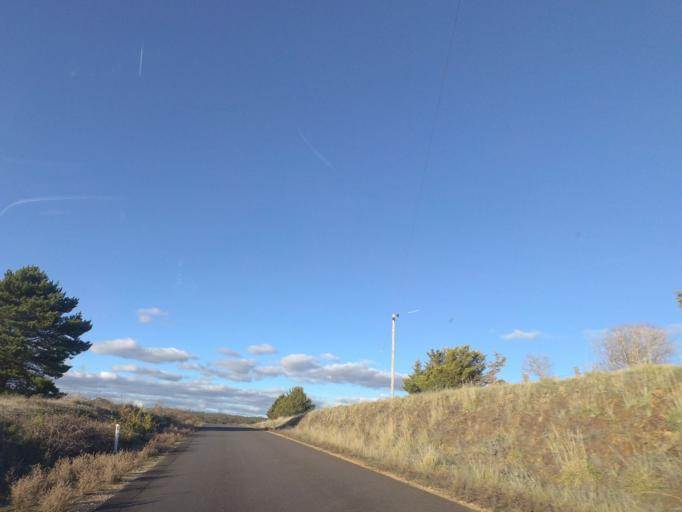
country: AU
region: Victoria
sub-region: Mount Alexander
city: Castlemaine
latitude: -37.1591
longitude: 144.2172
